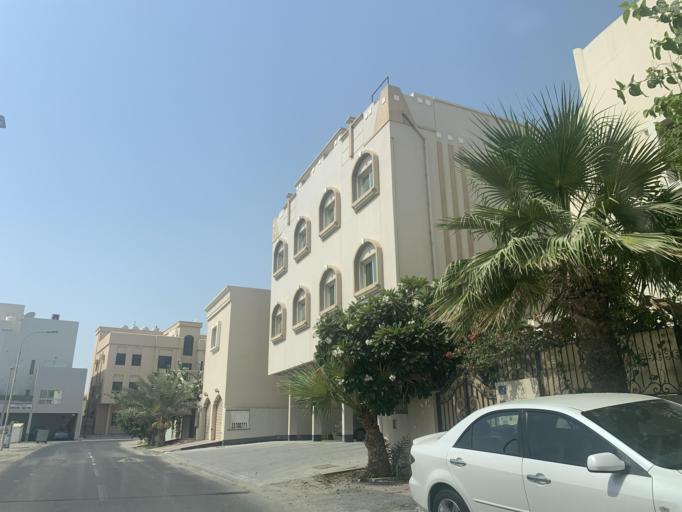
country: BH
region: Manama
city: Jidd Hafs
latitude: 26.2103
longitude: 50.5014
